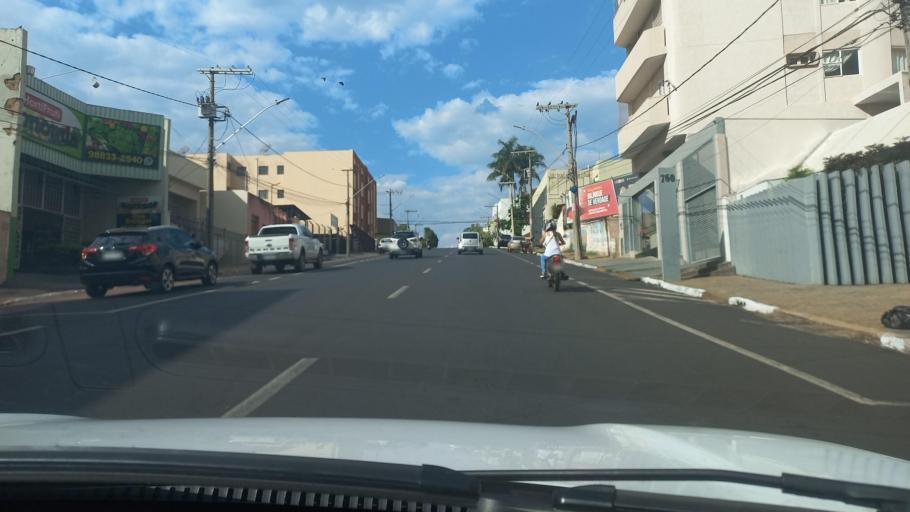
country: BR
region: Minas Gerais
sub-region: Uberaba
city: Uberaba
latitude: -19.7425
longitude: -47.9312
